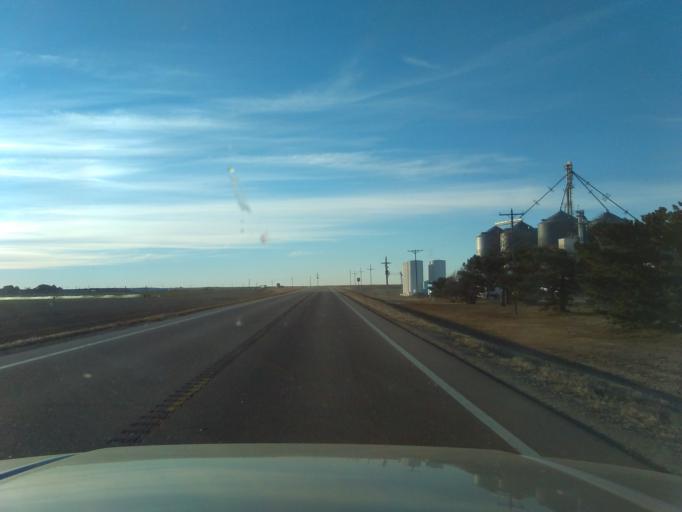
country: US
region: Kansas
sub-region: Thomas County
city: Colby
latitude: 39.4480
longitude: -100.8154
